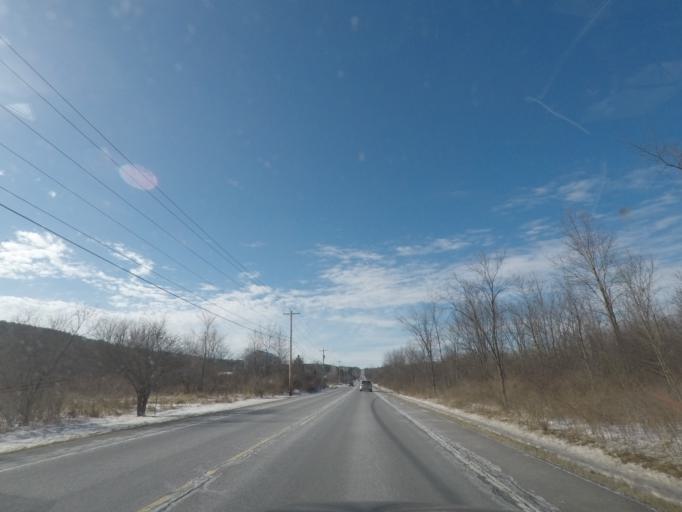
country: US
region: New York
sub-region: Albany County
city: Altamont
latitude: 42.7422
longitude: -74.0227
